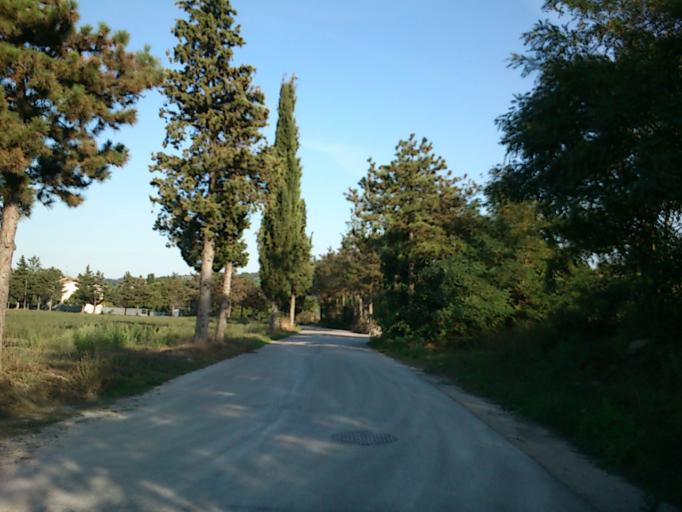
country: IT
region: The Marches
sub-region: Provincia di Pesaro e Urbino
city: Saltara
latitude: 43.7367
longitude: 12.9058
